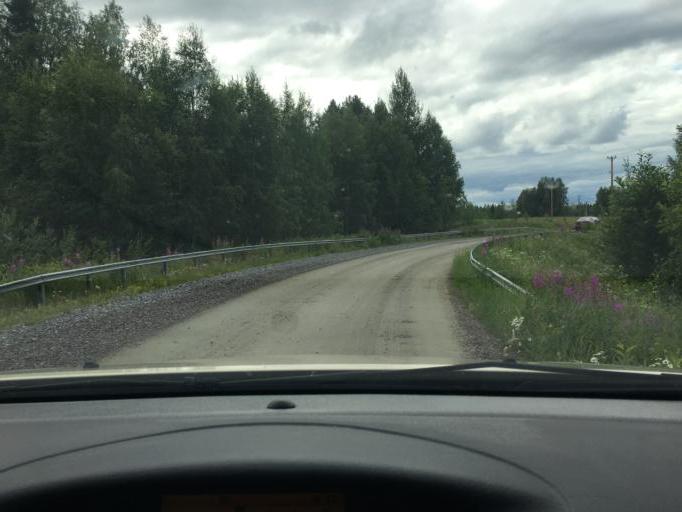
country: SE
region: Norrbotten
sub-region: Overkalix Kommun
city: OEverkalix
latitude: 66.0900
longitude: 22.8744
